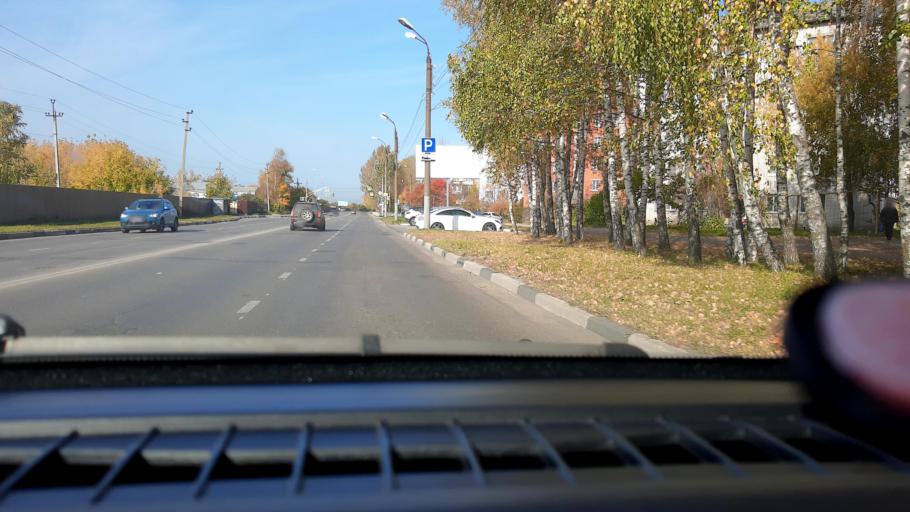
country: RU
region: Nizjnij Novgorod
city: Kstovo
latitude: 56.1417
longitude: 44.1843
